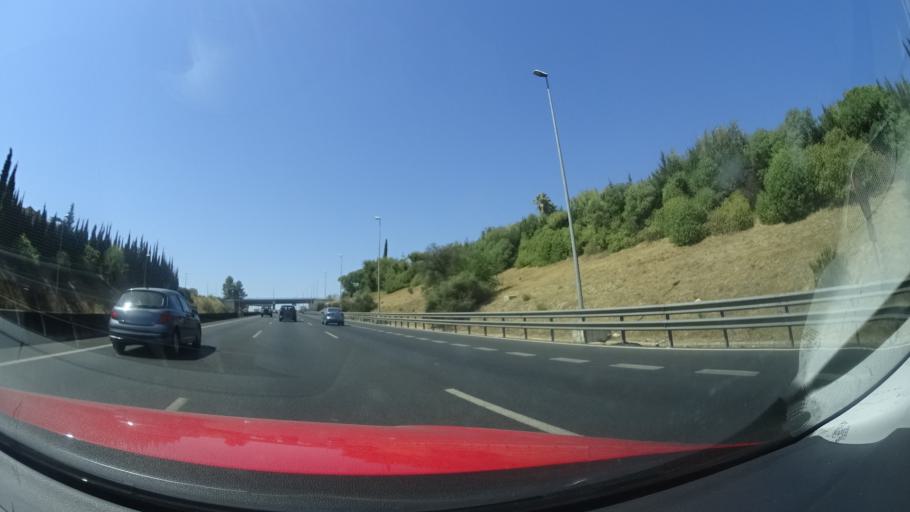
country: ES
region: Andalusia
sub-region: Provincia de Sevilla
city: Tomares
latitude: 37.3814
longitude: -6.0423
